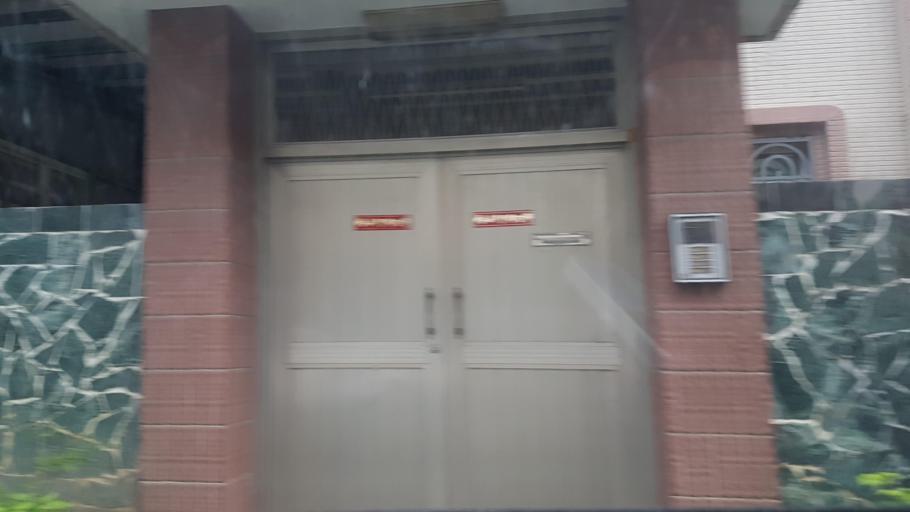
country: TW
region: Taiwan
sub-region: Hualien
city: Hualian
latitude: 23.9795
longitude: 121.5976
